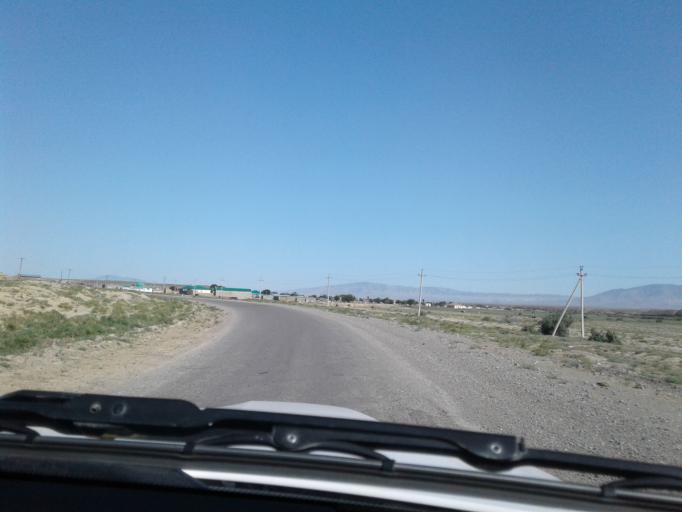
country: TM
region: Balkan
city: Serdar
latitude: 38.7135
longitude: 56.3280
